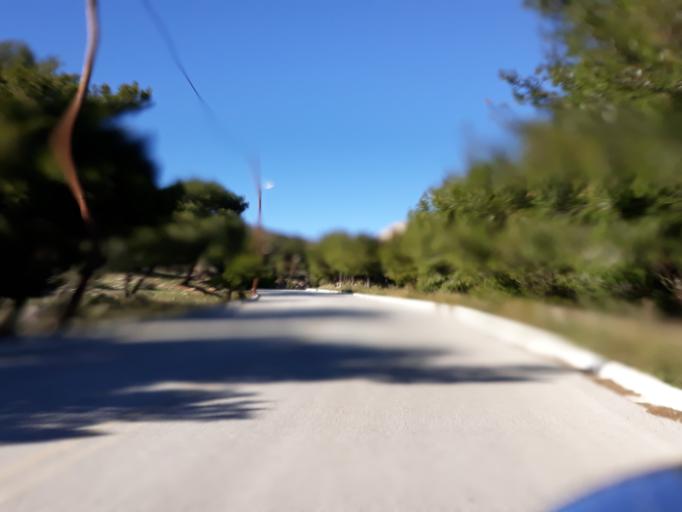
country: GR
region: Attica
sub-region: Nomarchia Dytikis Attikis
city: Fyli
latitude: 38.1036
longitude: 23.6812
